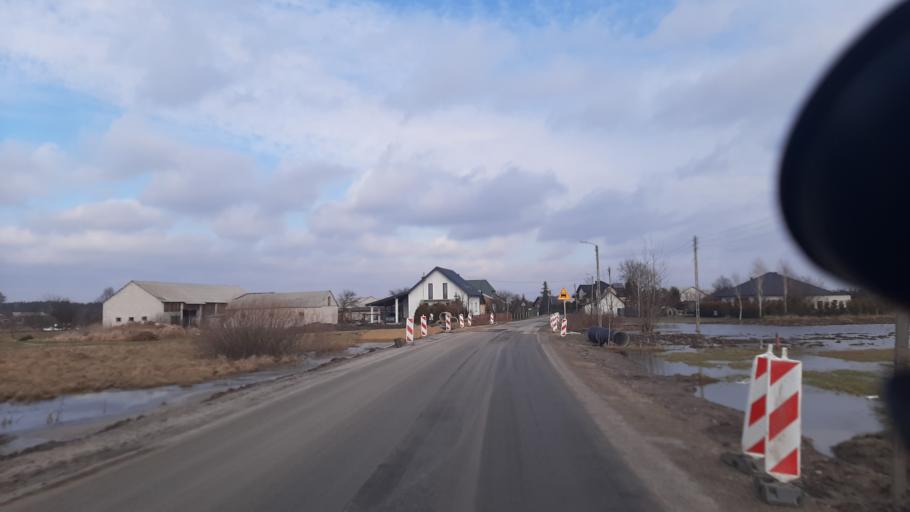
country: PL
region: Lublin Voivodeship
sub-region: Powiat lubartowski
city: Wola Sernicka
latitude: 51.4895
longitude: 22.7581
